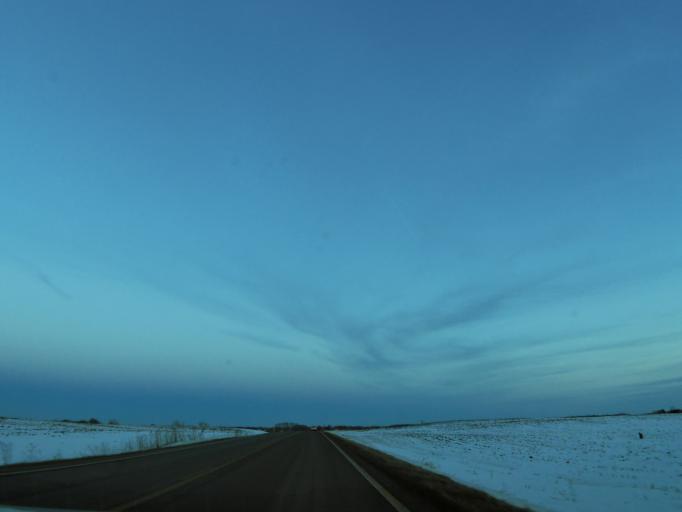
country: US
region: Minnesota
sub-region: Scott County
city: Shakopee
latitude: 44.7328
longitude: -93.5491
